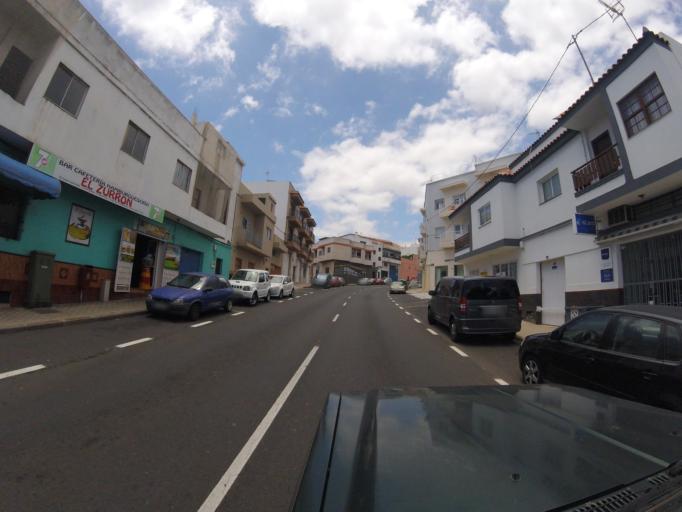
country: ES
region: Canary Islands
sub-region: Provincia de Santa Cruz de Tenerife
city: La Laguna
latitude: 28.4404
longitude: -16.3130
